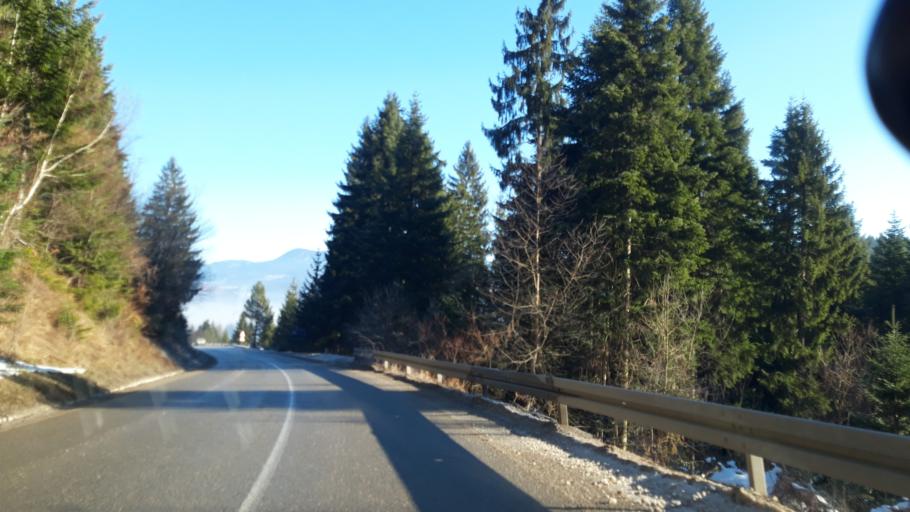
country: BA
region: Republika Srpska
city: Koran
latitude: 43.8040
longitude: 18.5521
